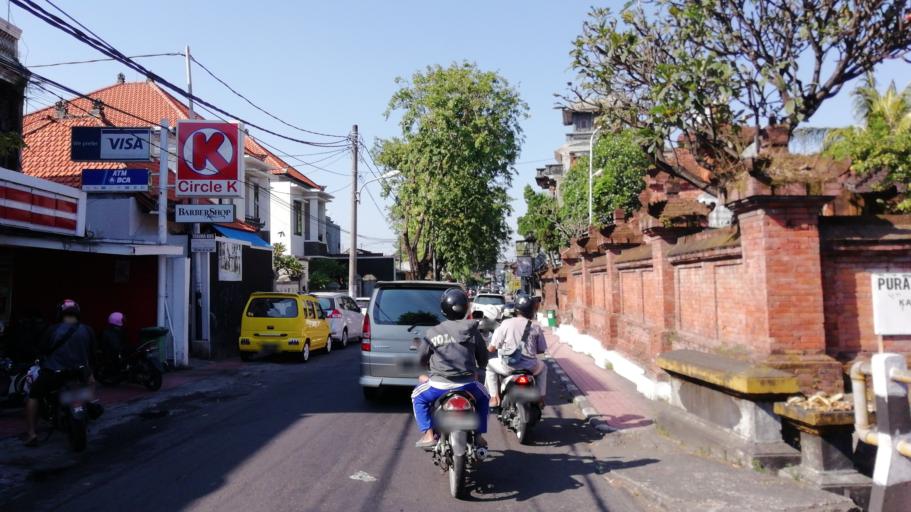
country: ID
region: Bali
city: Denpasar
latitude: -8.6591
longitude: 115.2198
